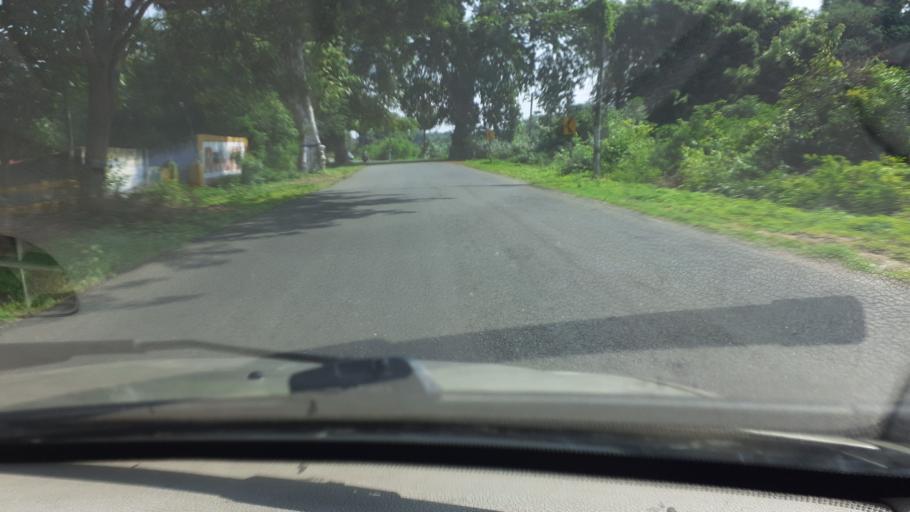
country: IN
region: Tamil Nadu
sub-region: Thoothukkudi
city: Srivaikuntam
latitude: 8.6326
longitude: 77.8859
